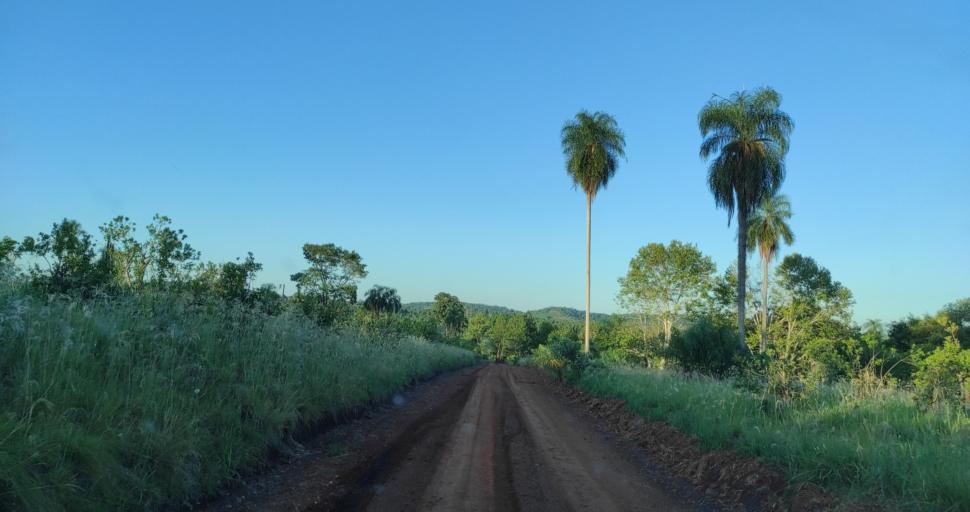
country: AR
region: Misiones
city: Gobernador Roca
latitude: -27.2177
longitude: -55.4146
